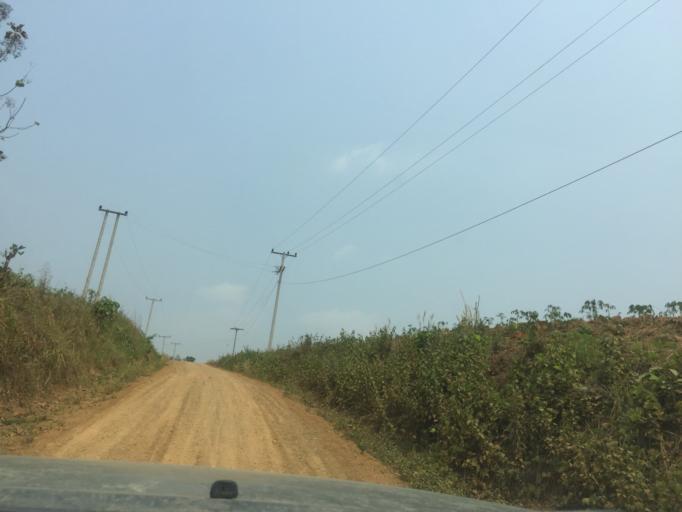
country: LA
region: Xiagnabouli
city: Muang Kenthao
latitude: 17.8070
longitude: 101.2702
